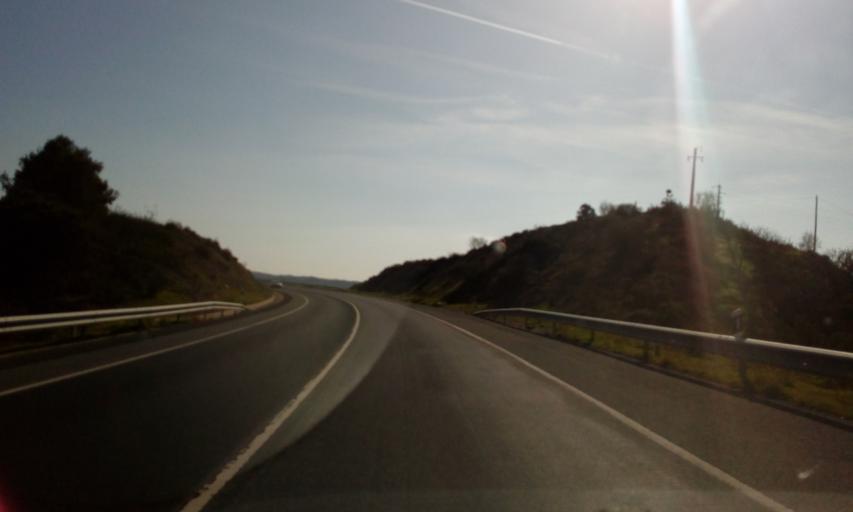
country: PT
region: Faro
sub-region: Castro Marim
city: Castro Marim
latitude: 37.2626
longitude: -7.4946
